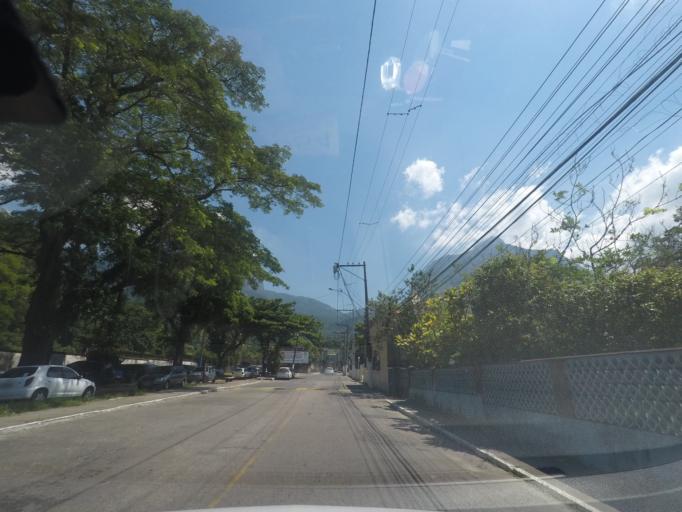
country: BR
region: Rio de Janeiro
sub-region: Petropolis
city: Petropolis
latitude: -22.5729
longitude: -43.1848
